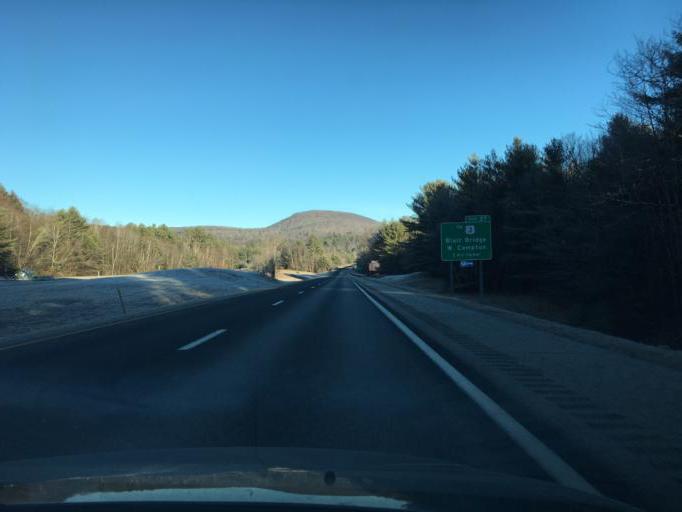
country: US
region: New Hampshire
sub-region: Grafton County
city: Plymouth
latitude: 43.7937
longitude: -71.6750
